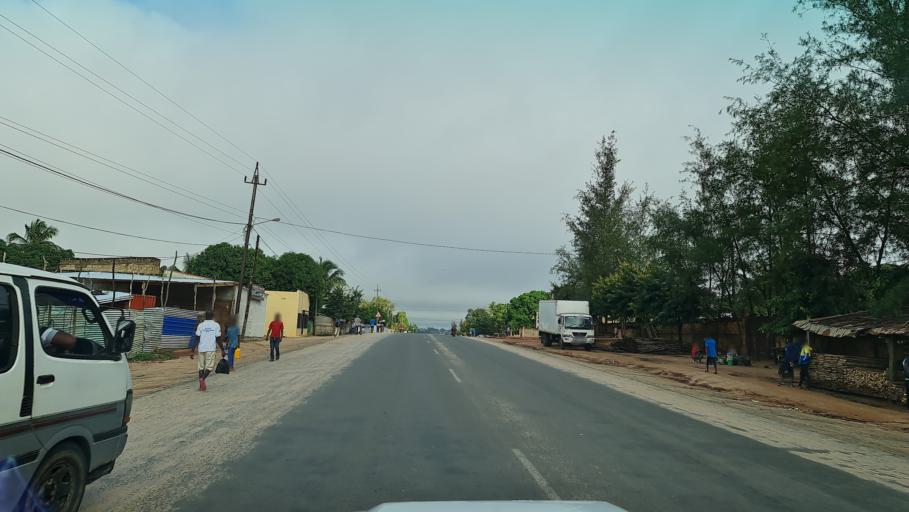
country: MZ
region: Nampula
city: Nampula
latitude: -15.1370
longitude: 39.2821
